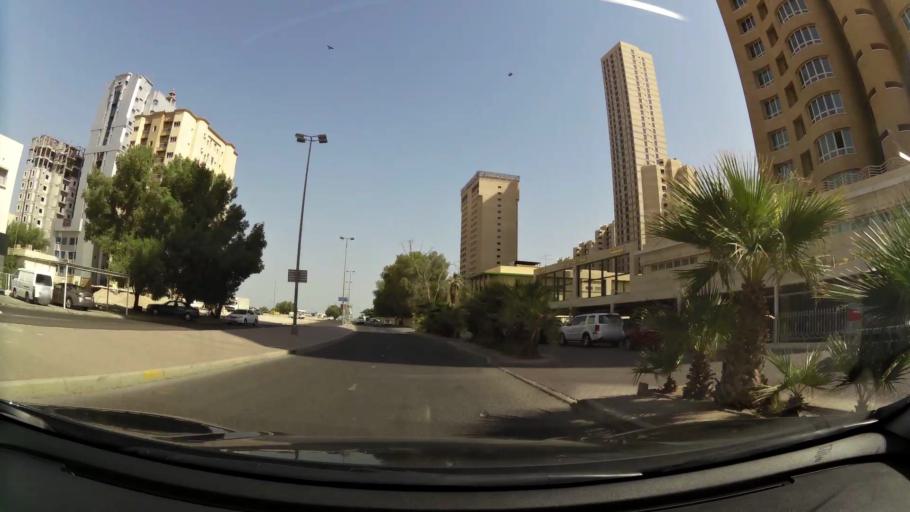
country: KW
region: Al Asimah
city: Ad Dasmah
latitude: 29.3771
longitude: 47.9994
